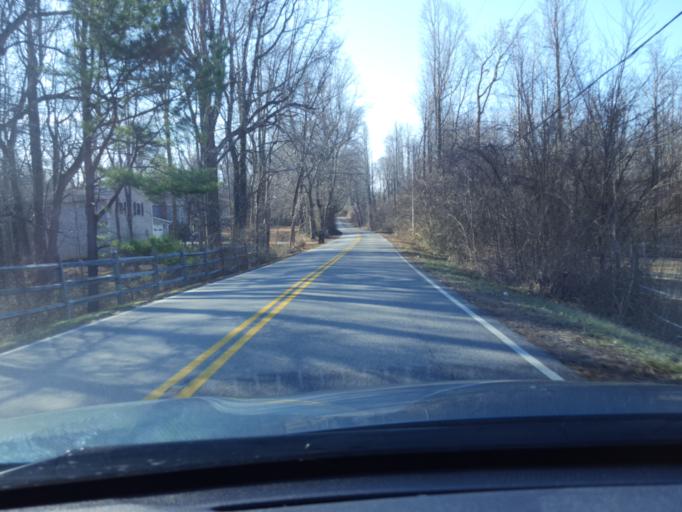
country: US
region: Maryland
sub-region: Calvert County
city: Chesapeake Beach
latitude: 38.6428
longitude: -76.5409
